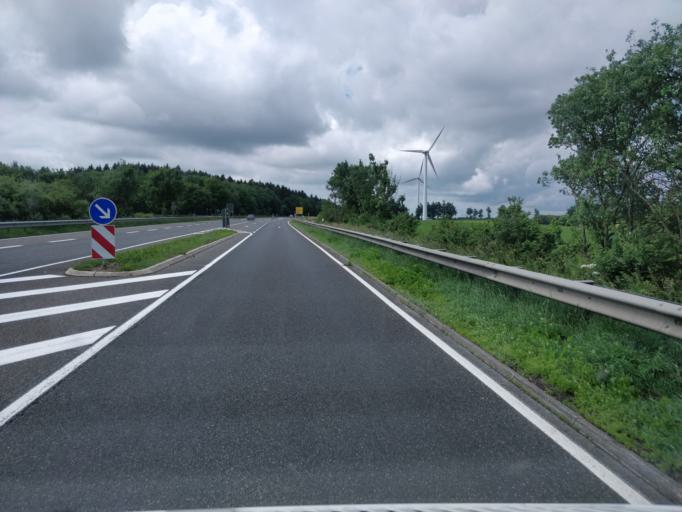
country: DE
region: North Rhine-Westphalia
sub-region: Regierungsbezirk Koln
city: Blankenheim
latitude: 50.4297
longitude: 6.6068
